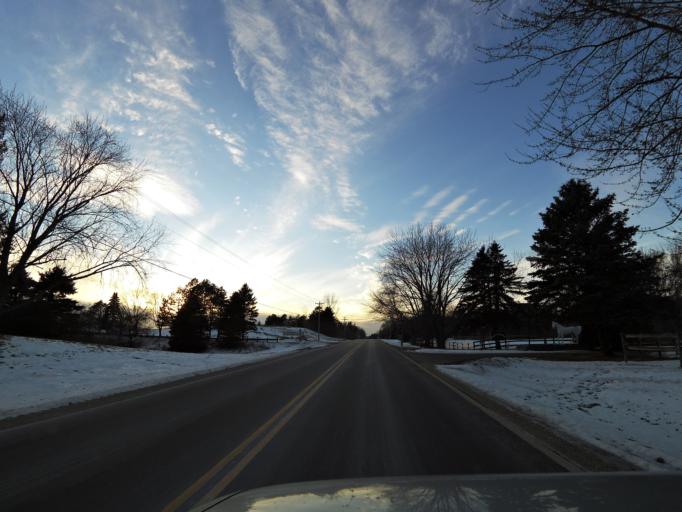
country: US
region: Minnesota
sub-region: Washington County
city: Lake Elmo
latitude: 44.9781
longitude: -92.8687
